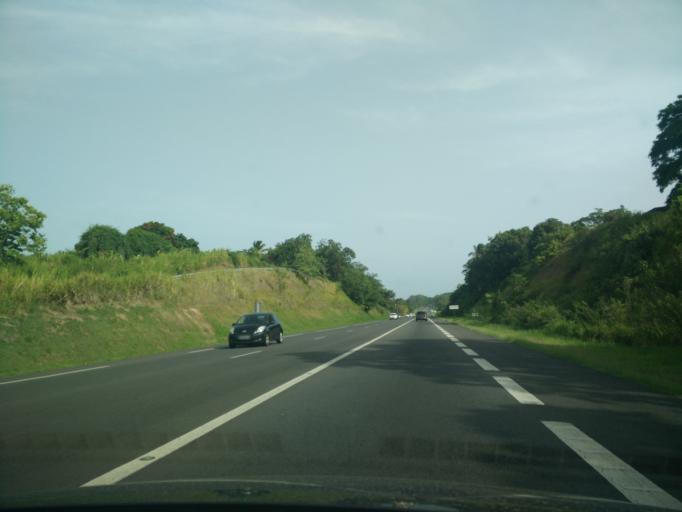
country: GP
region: Guadeloupe
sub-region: Guadeloupe
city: Petit-Bourg
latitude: 16.1547
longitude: -61.5853
